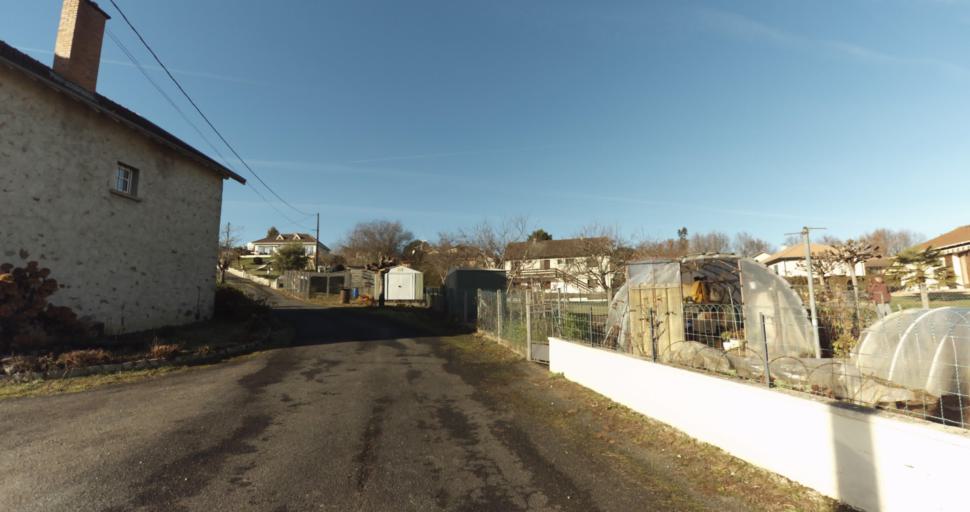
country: FR
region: Limousin
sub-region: Departement de la Haute-Vienne
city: Aixe-sur-Vienne
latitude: 45.8016
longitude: 1.1491
